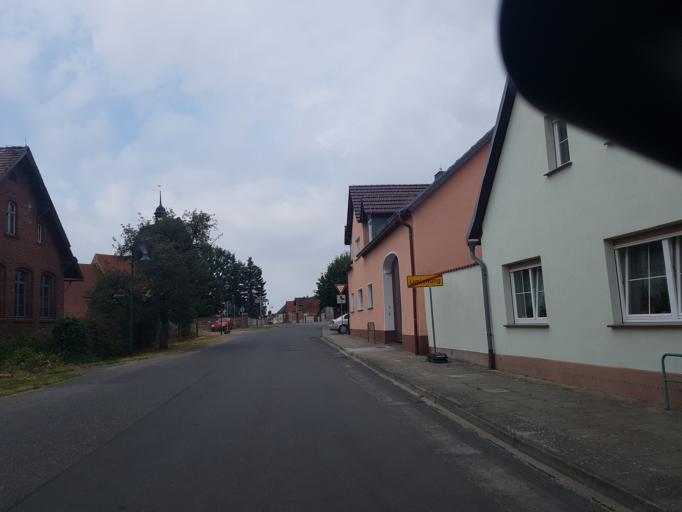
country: DE
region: Brandenburg
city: Doberlug-Kirchhain
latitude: 51.6907
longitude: 13.5137
